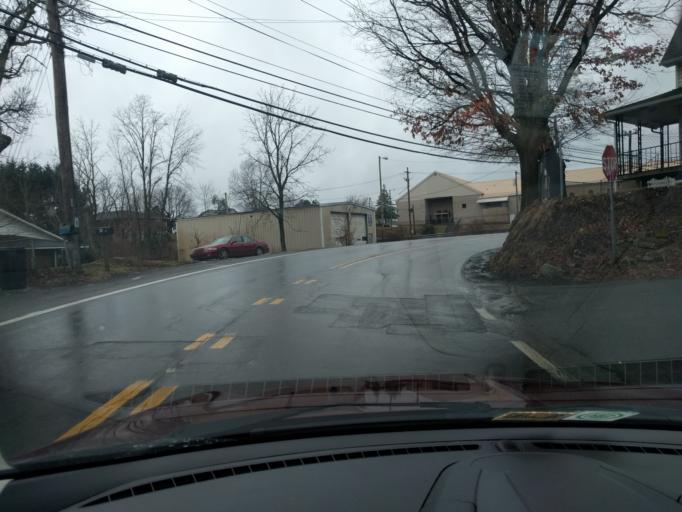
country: US
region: West Virginia
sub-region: Raleigh County
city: Beckley
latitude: 37.7927
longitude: -81.1816
